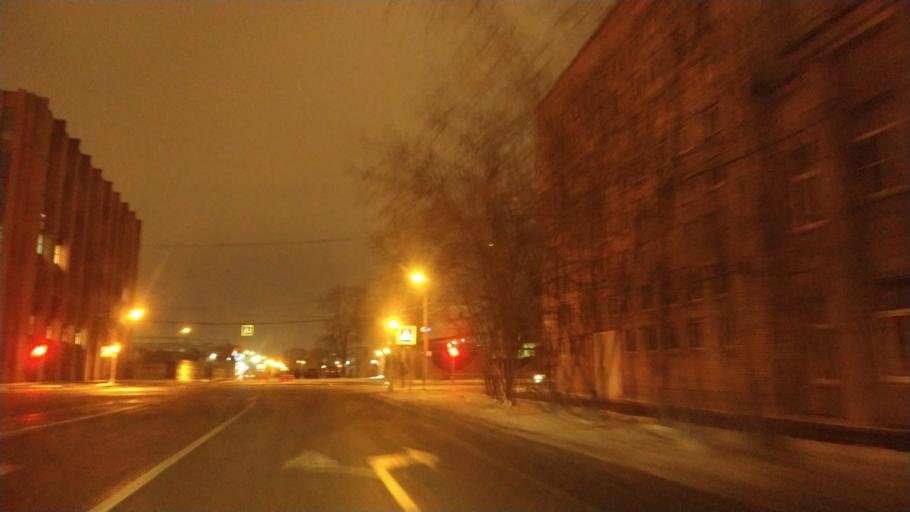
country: RU
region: St.-Petersburg
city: Kupchino
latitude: 59.8814
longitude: 30.3390
